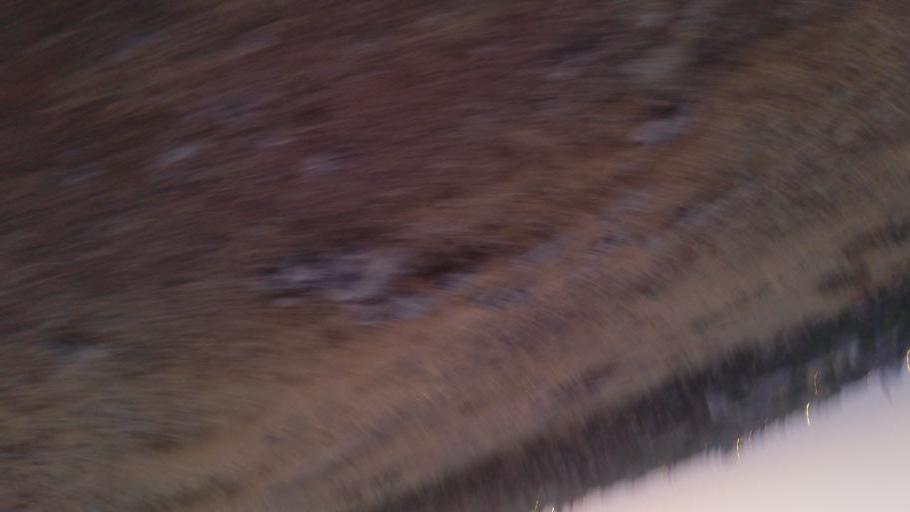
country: TR
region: Mardin
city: Kindirip
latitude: 37.4481
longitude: 41.2254
